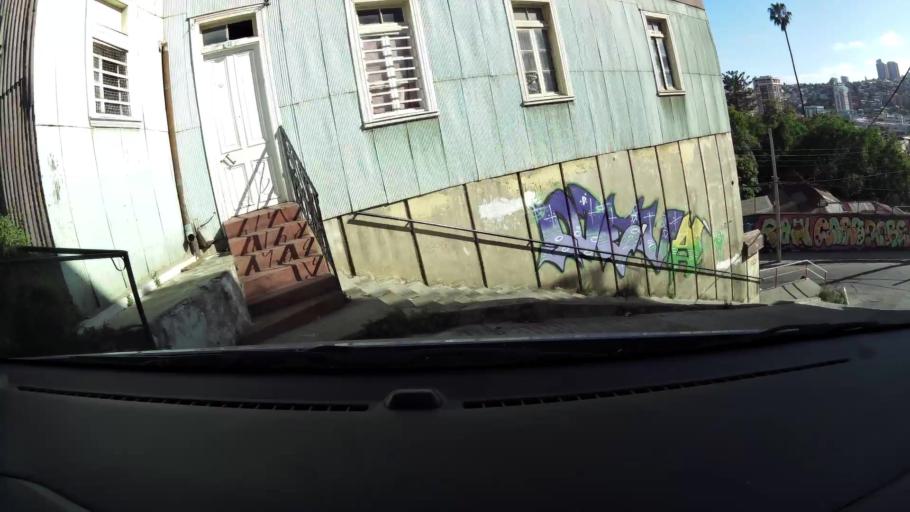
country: CL
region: Valparaiso
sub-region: Provincia de Valparaiso
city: Valparaiso
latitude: -33.0531
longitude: -71.6094
